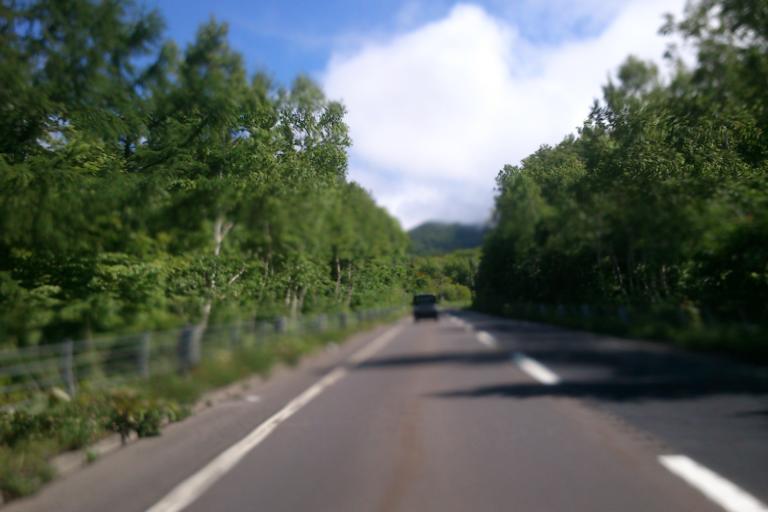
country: JP
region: Hokkaido
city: Ishikari
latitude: 43.5090
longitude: 141.3747
